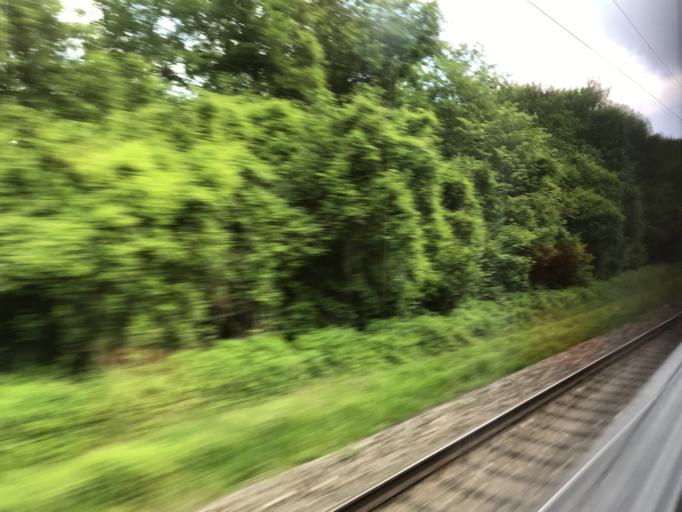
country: DE
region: Bavaria
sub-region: Swabia
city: Leipheim
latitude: 48.4532
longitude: 10.2227
